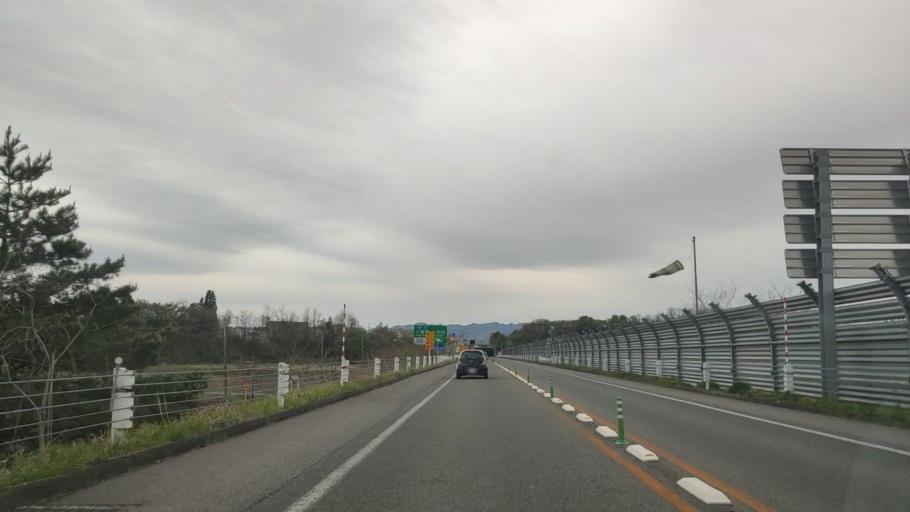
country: JP
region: Akita
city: Odate
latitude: 40.2800
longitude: 140.5380
